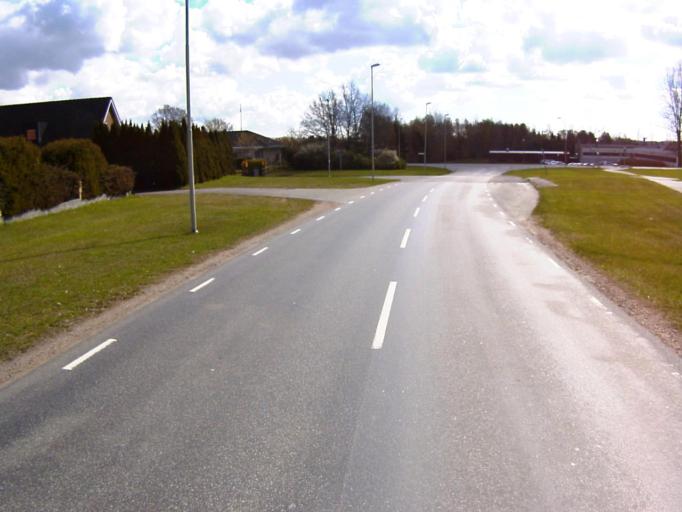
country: SE
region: Skane
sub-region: Kristianstads Kommun
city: Kristianstad
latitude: 56.0104
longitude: 14.0998
